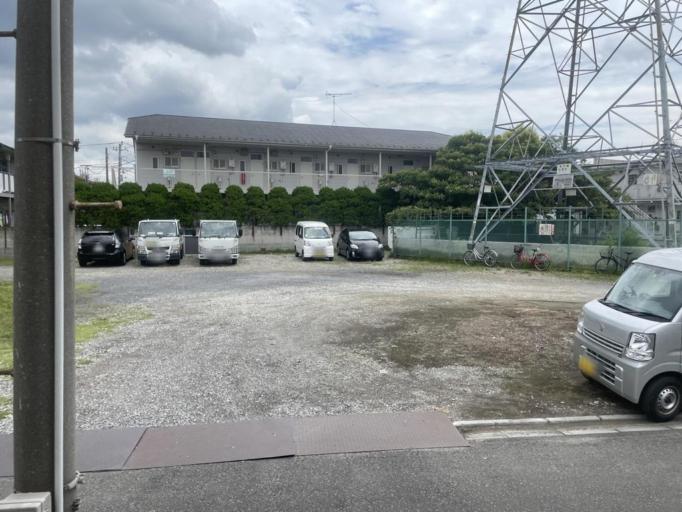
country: JP
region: Chiba
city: Matsudo
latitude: 35.7550
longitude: 139.8740
